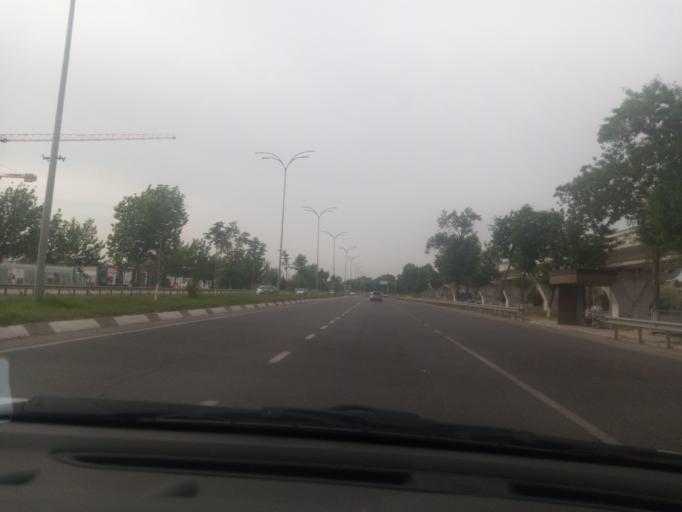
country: UZ
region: Toshkent Shahri
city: Bektemir
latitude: 41.2762
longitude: 69.3616
